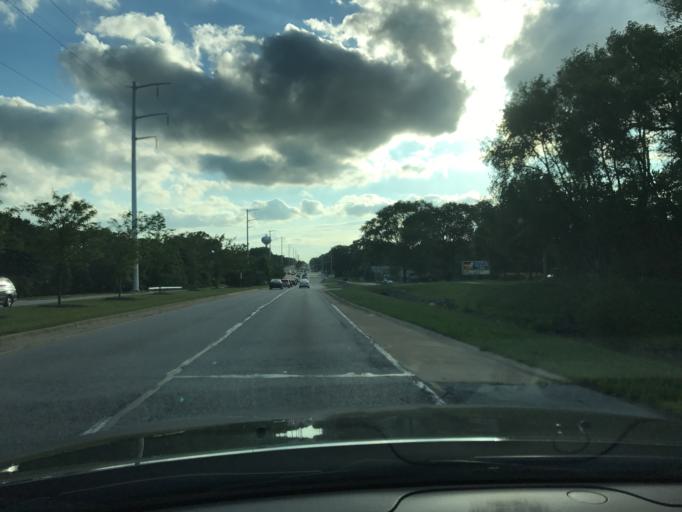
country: US
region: Illinois
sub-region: DuPage County
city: Naperville
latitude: 41.7486
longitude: -88.1243
